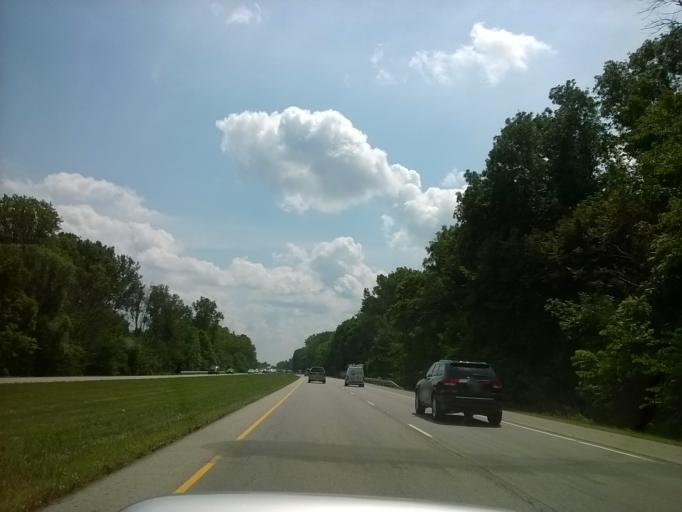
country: US
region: Indiana
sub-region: Hamilton County
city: Carmel
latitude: 39.9493
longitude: -86.1140
